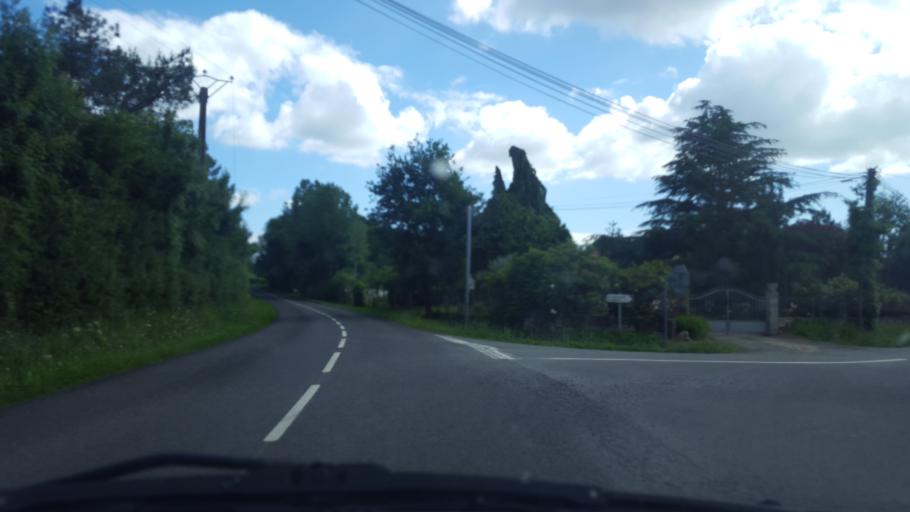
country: FR
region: Pays de la Loire
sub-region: Departement de la Loire-Atlantique
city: Saint-Lumine-de-Coutais
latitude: 47.0388
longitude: -1.7378
